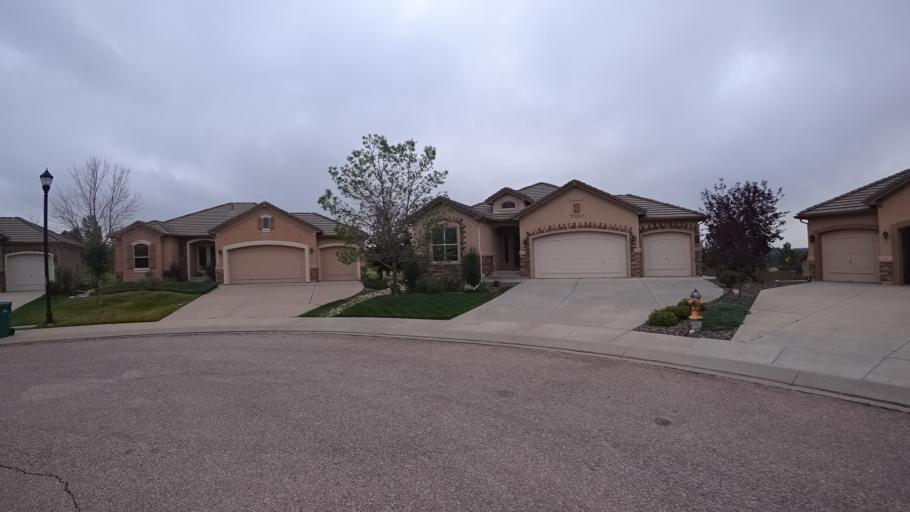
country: US
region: Colorado
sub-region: El Paso County
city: Gleneagle
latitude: 39.0311
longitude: -104.7782
